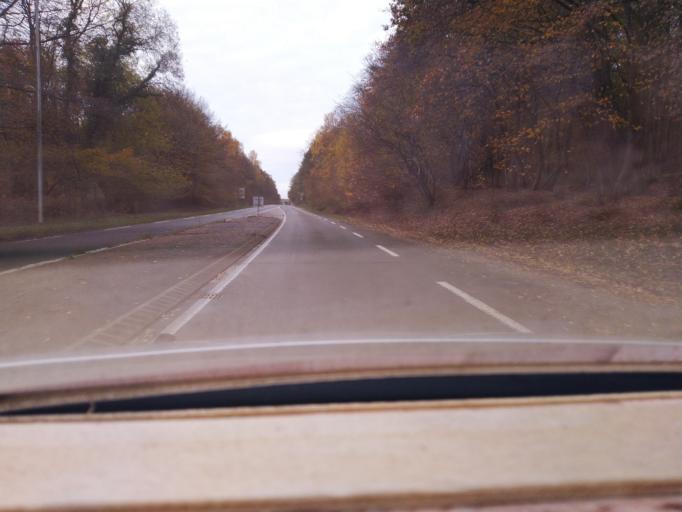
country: FR
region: Haute-Normandie
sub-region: Departement de la Seine-Maritime
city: Canteleu
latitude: 49.4451
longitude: 1.0114
